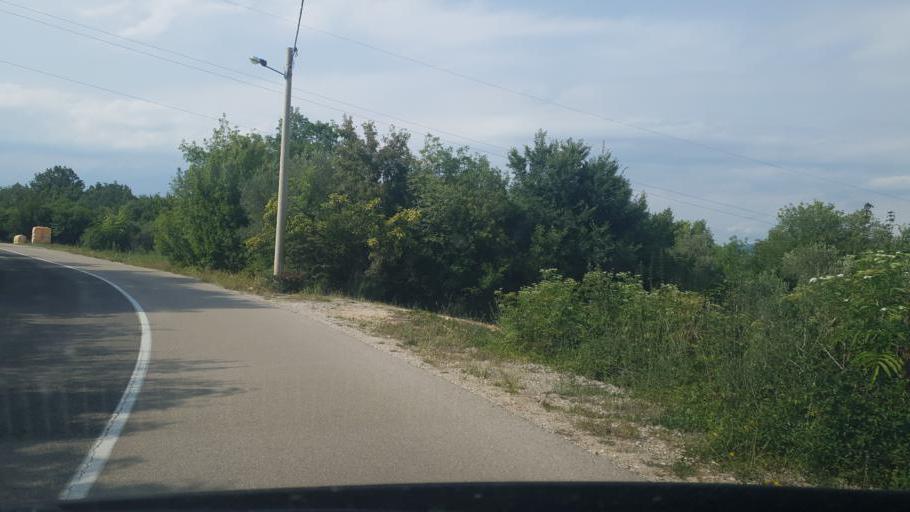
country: HR
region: Primorsko-Goranska
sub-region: Grad Crikvenica
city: Crikvenica
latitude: 45.1387
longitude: 14.6208
